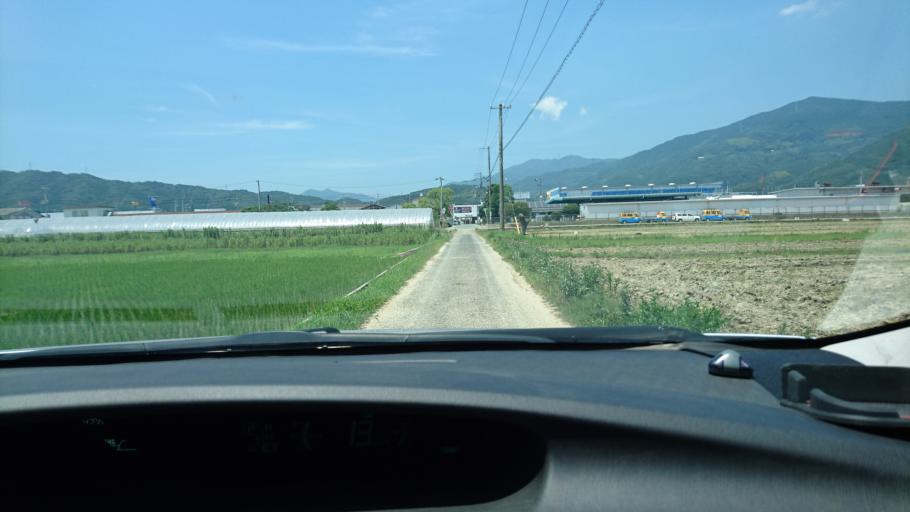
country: JP
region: Ehime
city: Ozu
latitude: 33.5258
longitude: 132.5675
